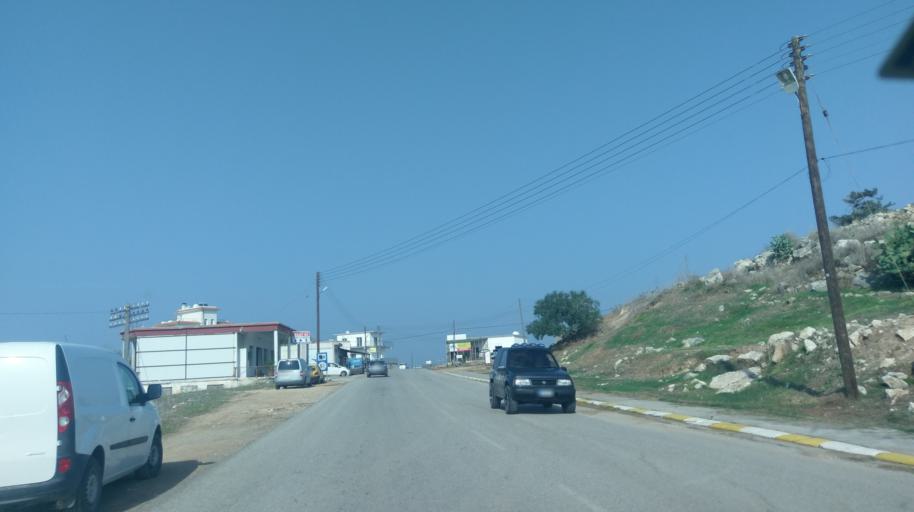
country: CY
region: Ammochostos
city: Leonarisso
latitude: 35.5072
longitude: 34.1607
